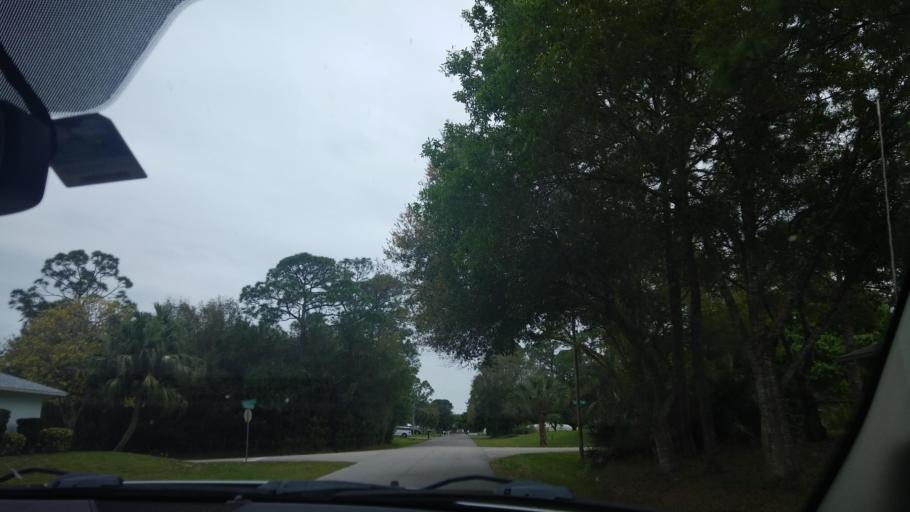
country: US
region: Florida
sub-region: Indian River County
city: Sebastian
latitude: 27.7605
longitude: -80.4923
